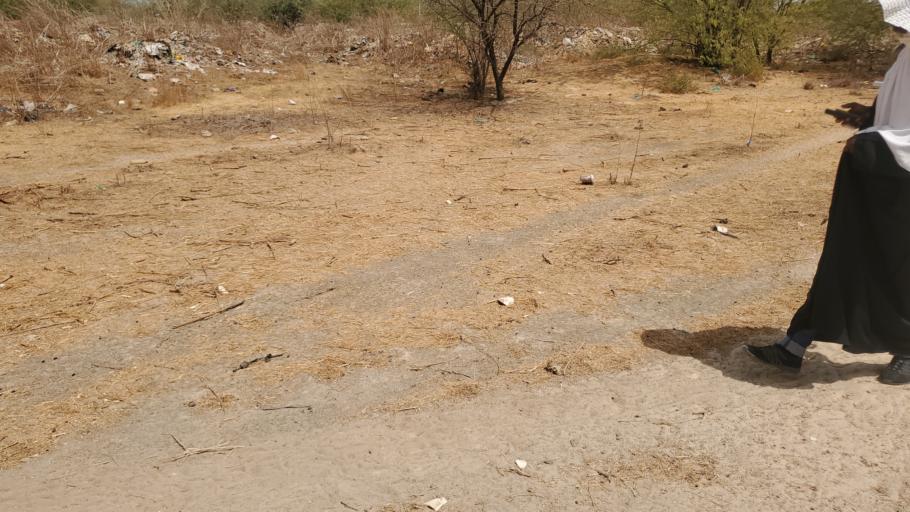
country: SN
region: Saint-Louis
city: Saint-Louis
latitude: 15.9510
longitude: -16.4346
